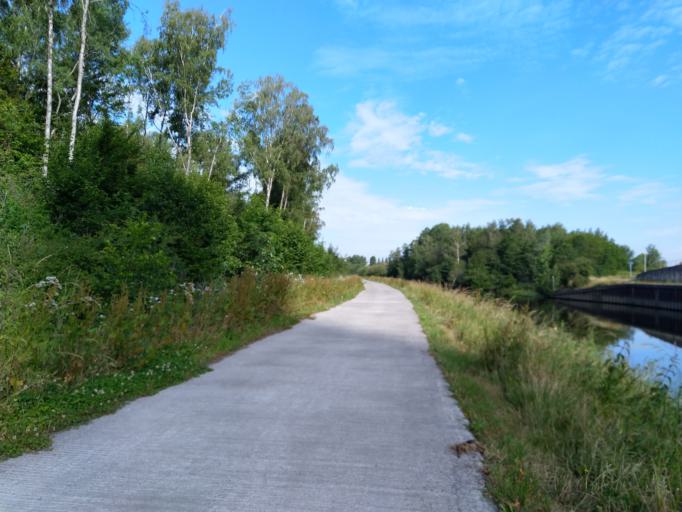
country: FR
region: Nord-Pas-de-Calais
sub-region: Departement du Nord
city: Recquignies
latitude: 50.2810
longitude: 4.0227
